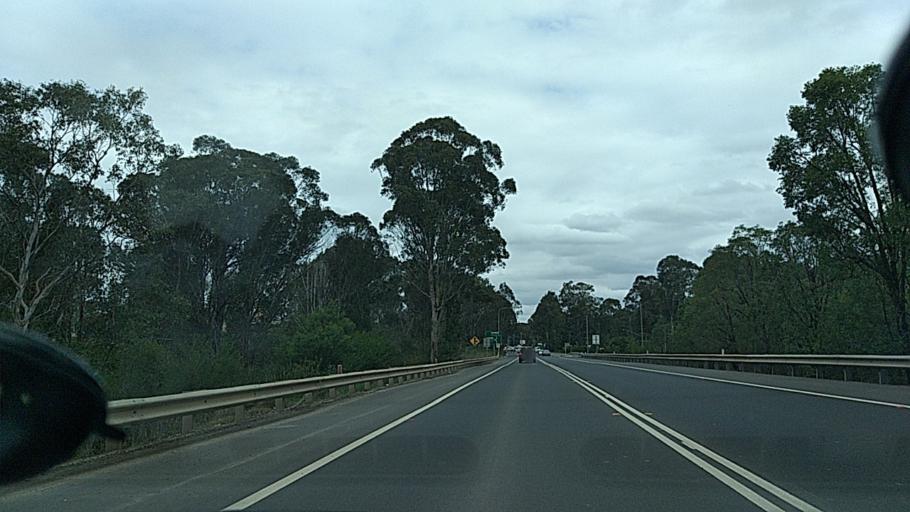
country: AU
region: New South Wales
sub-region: Hawkesbury
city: South Windsor
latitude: -33.6367
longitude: 150.7816
